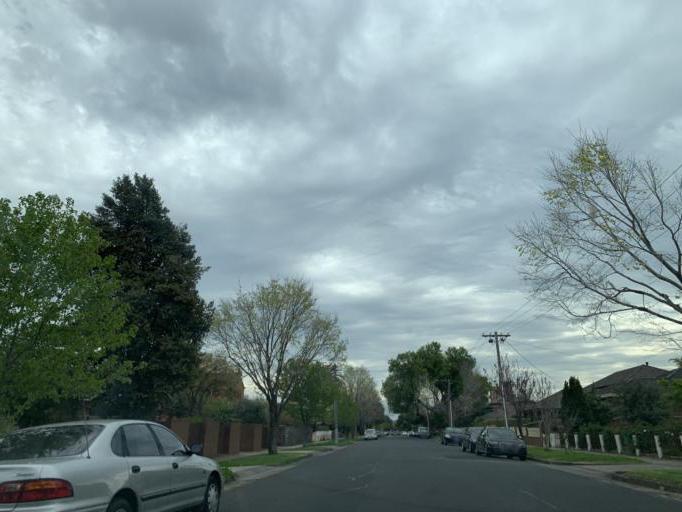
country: AU
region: Victoria
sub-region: Moreland
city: Coburg
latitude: -37.7523
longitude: 144.9733
